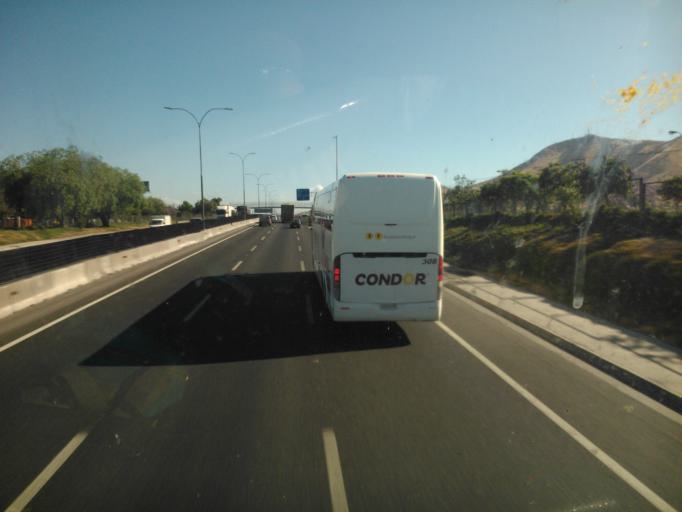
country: CL
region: Santiago Metropolitan
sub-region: Provincia de Maipo
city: San Bernardo
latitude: -33.5754
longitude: -70.7131
